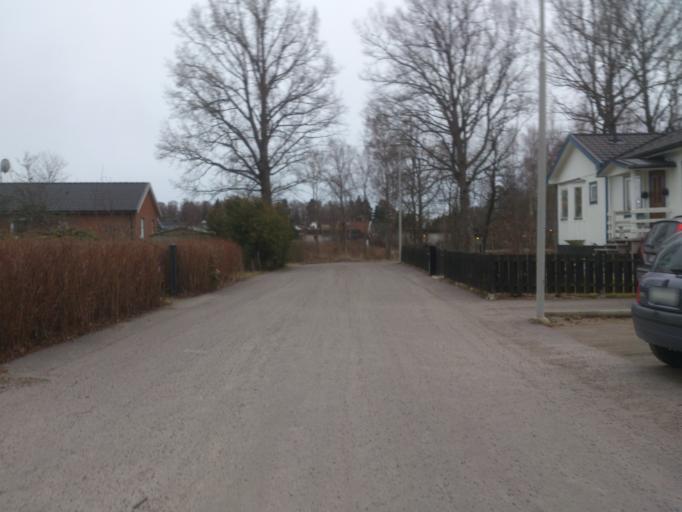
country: SE
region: OEstergoetland
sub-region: Linkopings Kommun
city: Malmslatt
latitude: 58.3978
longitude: 15.5415
